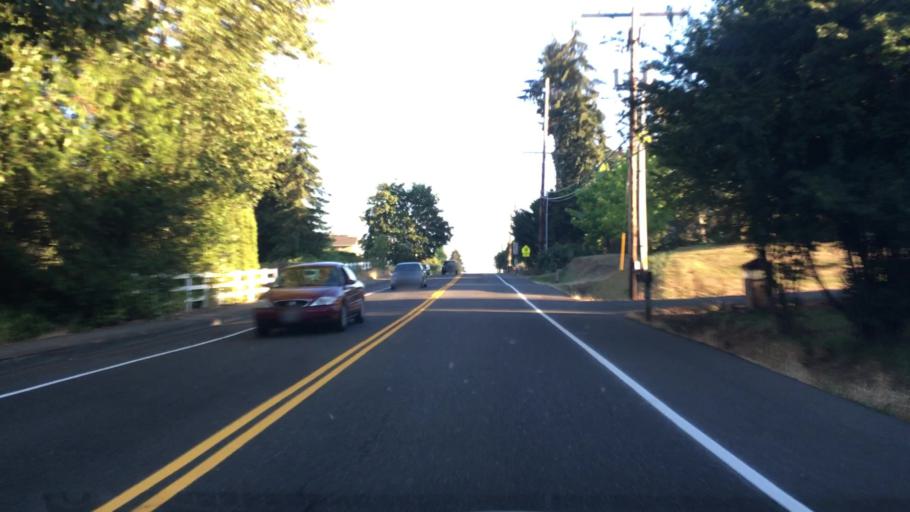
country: US
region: Washington
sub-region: King County
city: Lea Hill
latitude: 47.3278
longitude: -122.1764
